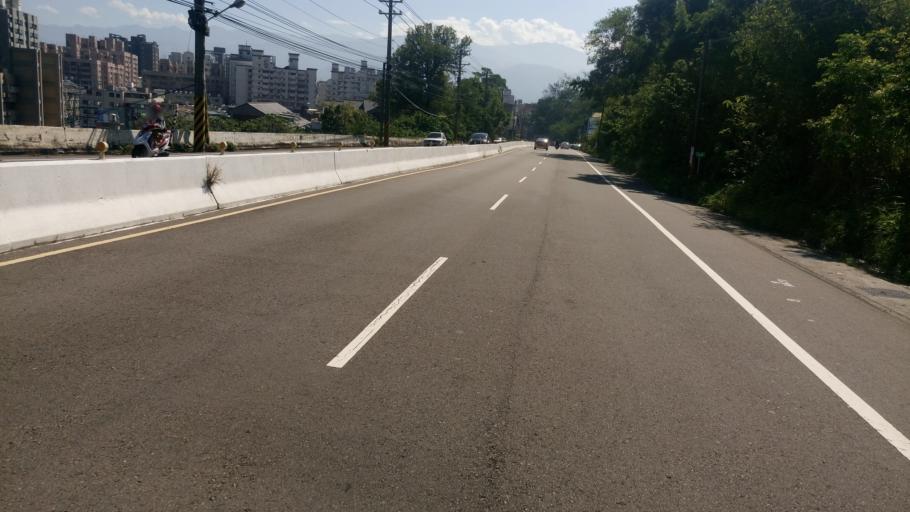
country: TW
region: Taiwan
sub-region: Hsinchu
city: Zhubei
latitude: 24.7507
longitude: 121.0780
